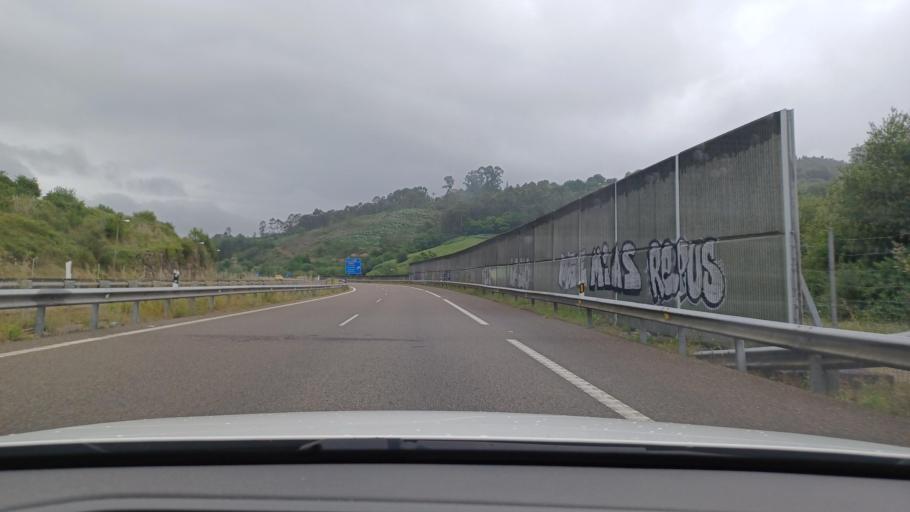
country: ES
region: Asturias
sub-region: Province of Asturias
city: Lugones
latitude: 43.4772
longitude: -5.7559
